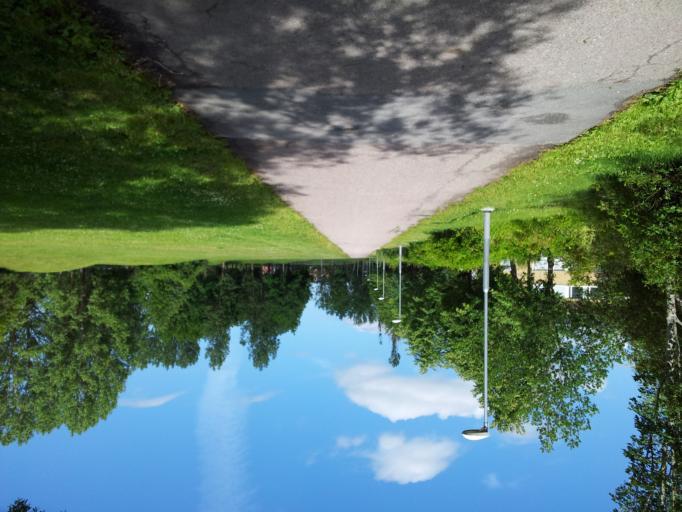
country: SE
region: Uppsala
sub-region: Uppsala Kommun
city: Uppsala
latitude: 59.8736
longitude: 17.6630
